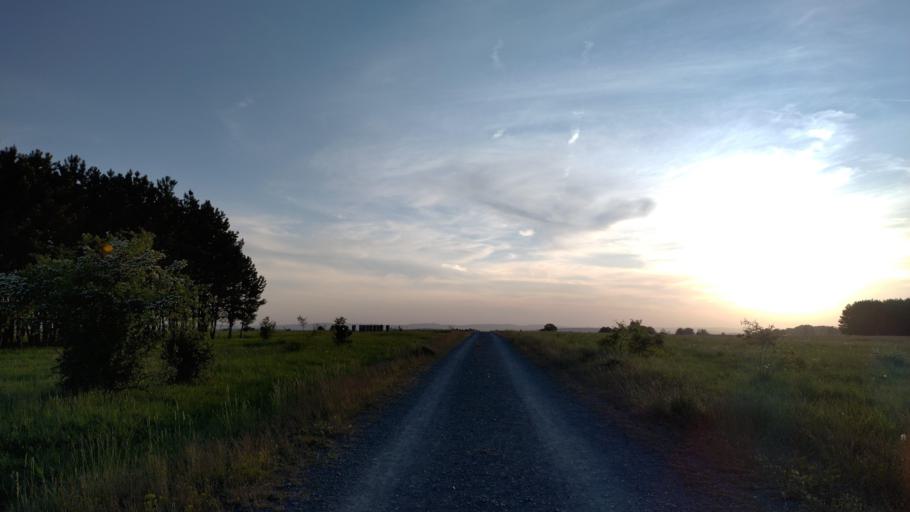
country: DE
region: Bavaria
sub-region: Upper Franconia
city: Bindlach
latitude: 49.9875
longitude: 11.6368
